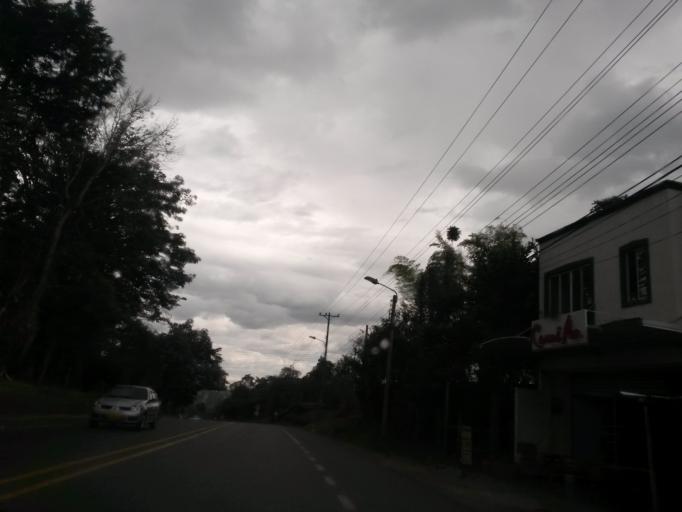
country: CO
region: Cauca
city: Popayan
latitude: 2.5075
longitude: -76.5486
